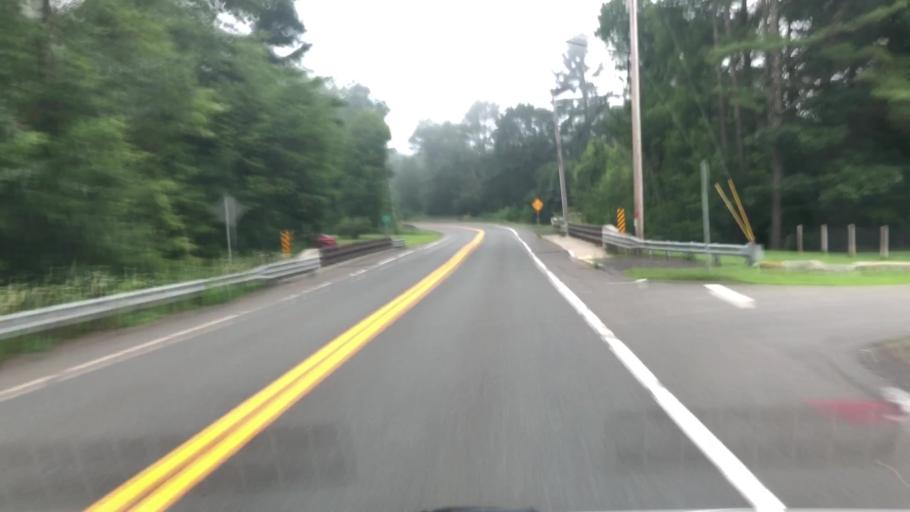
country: US
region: Massachusetts
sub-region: Franklin County
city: Shelburne Falls
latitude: 42.6135
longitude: -72.7671
